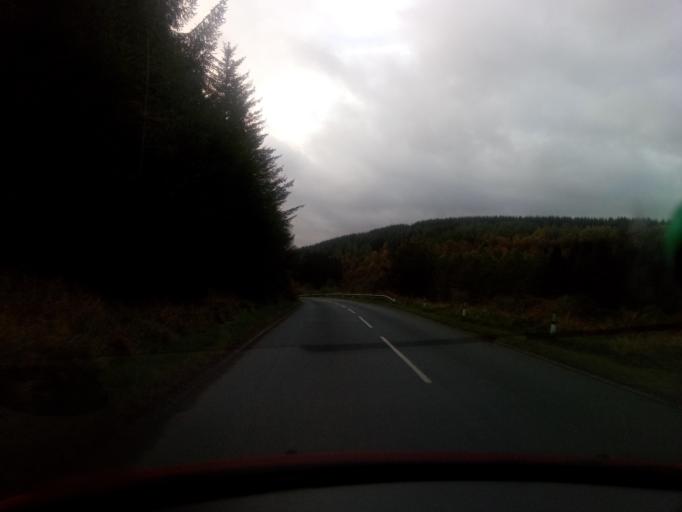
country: GB
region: Scotland
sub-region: The Scottish Borders
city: Hawick
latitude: 55.3630
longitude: -2.6503
